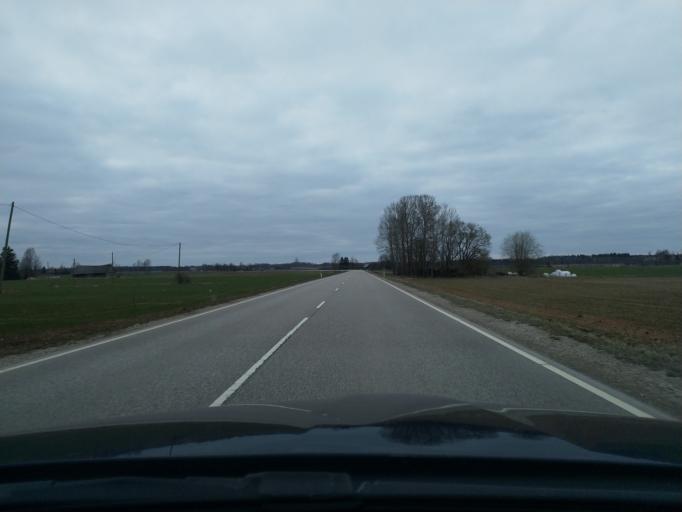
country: LV
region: Talsu Rajons
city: Sabile
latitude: 56.9325
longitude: 22.5191
